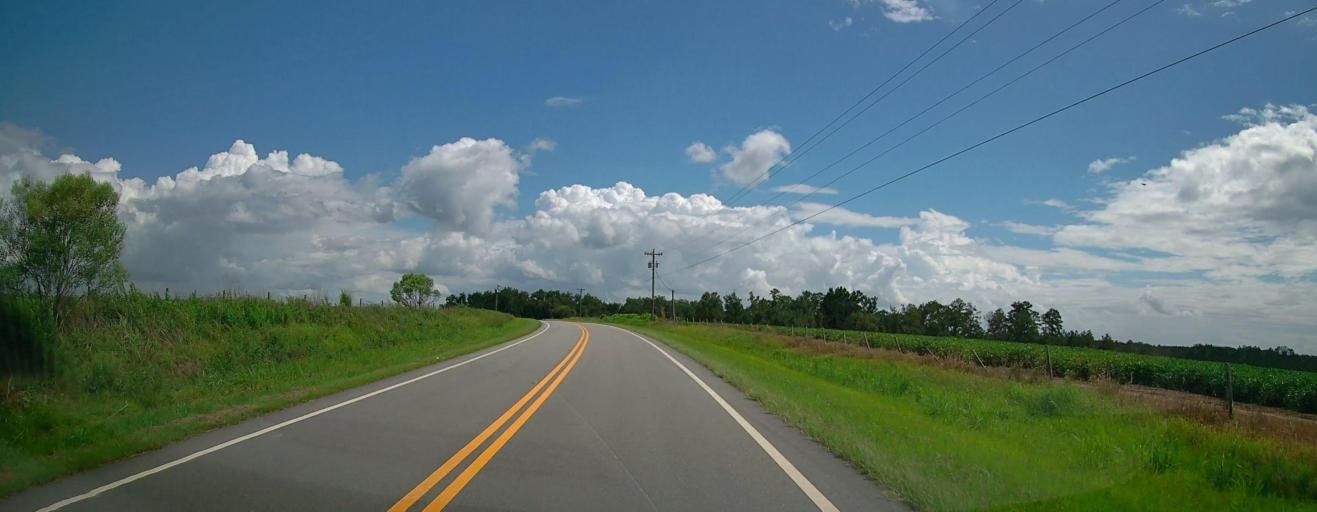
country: US
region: Georgia
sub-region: Irwin County
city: Ocilla
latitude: 31.6050
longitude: -83.1660
